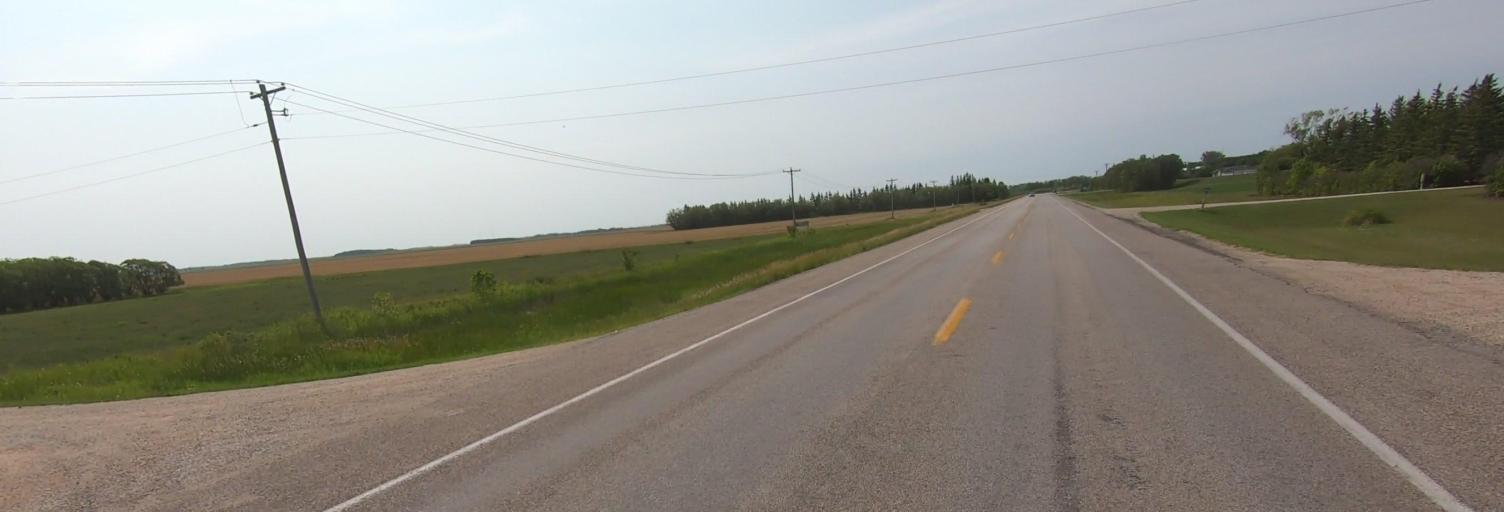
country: CA
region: Manitoba
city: Niverville
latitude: 49.6408
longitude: -97.1056
